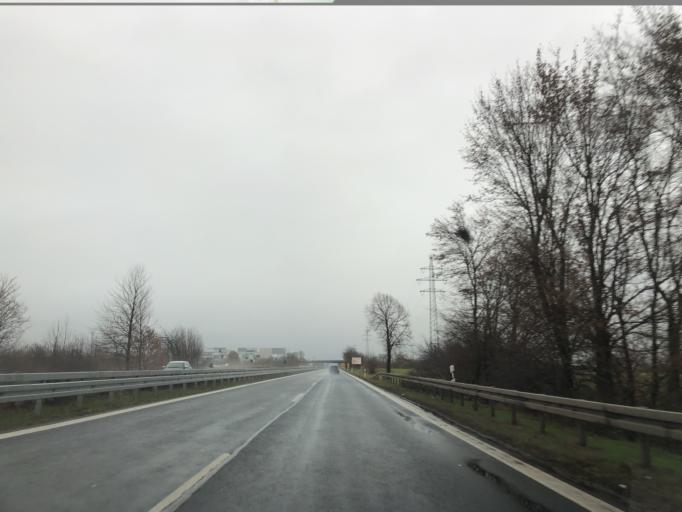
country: DE
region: Bavaria
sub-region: Regierungsbezirk Unterfranken
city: Niedernberg
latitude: 49.9194
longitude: 9.1115
